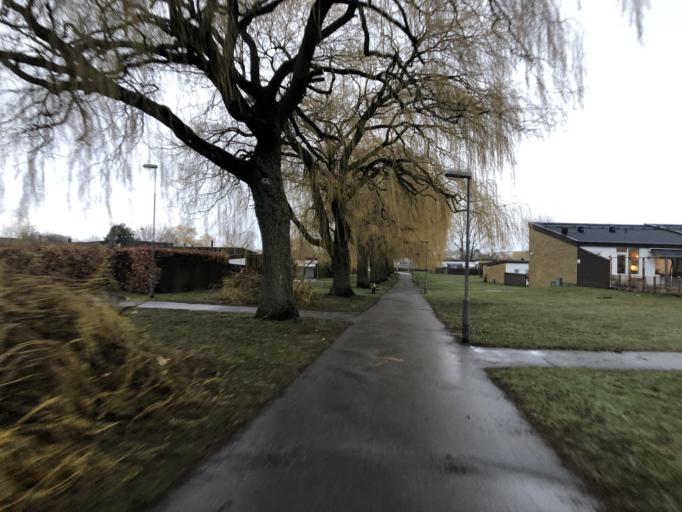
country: SE
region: Skane
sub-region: Burlovs Kommun
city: Arloev
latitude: 55.5873
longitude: 13.0657
